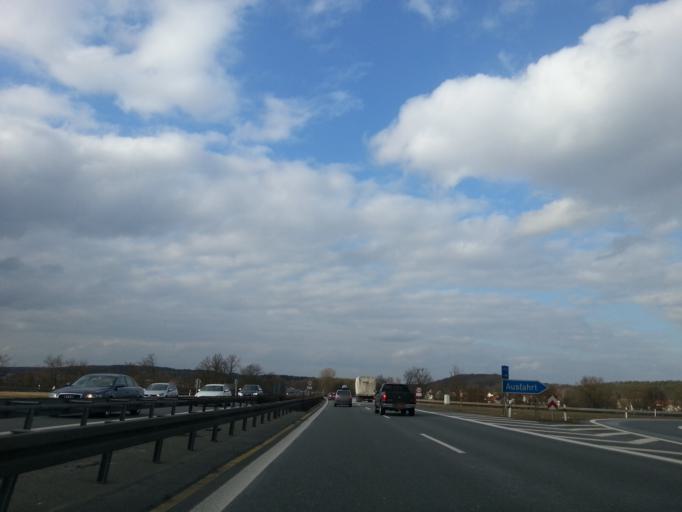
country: DE
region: Bavaria
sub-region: Regierungsbezirk Mittelfranken
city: Gremsdorf
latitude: 49.6998
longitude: 10.8552
